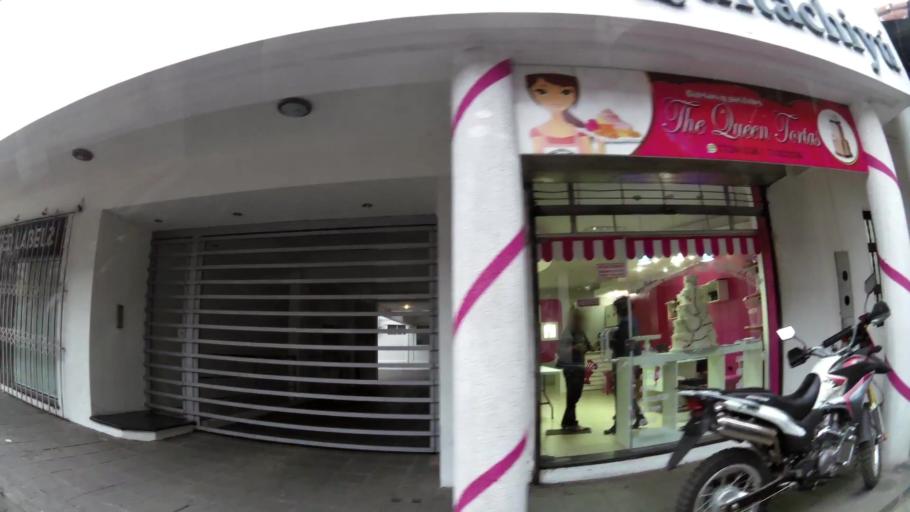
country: BO
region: Santa Cruz
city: Santa Cruz de la Sierra
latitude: -17.7842
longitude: -63.1803
